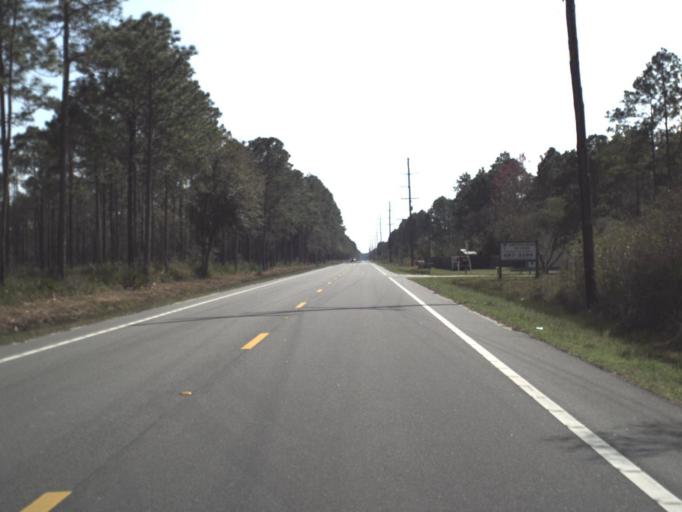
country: US
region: Florida
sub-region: Wakulla County
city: Crawfordville
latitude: 30.0406
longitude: -84.4957
